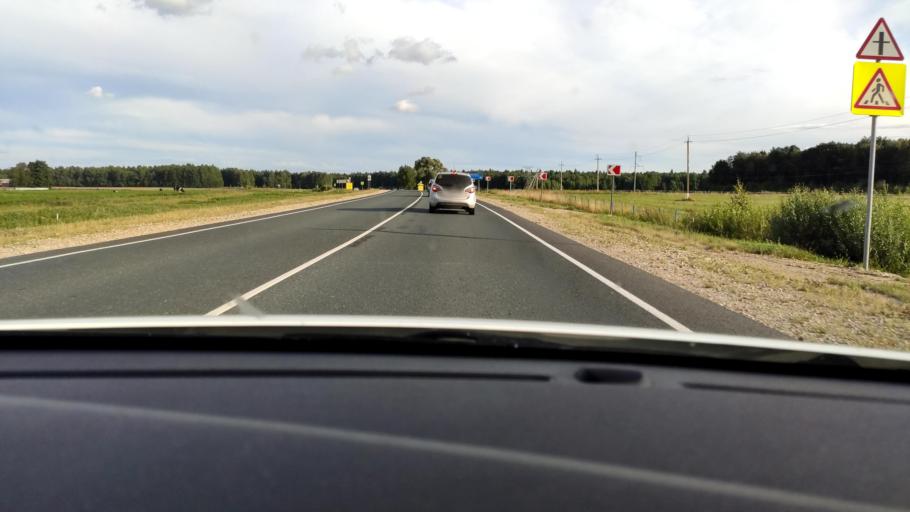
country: RU
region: Mariy-El
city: Krasnogorskiy
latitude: 56.1944
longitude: 48.2370
